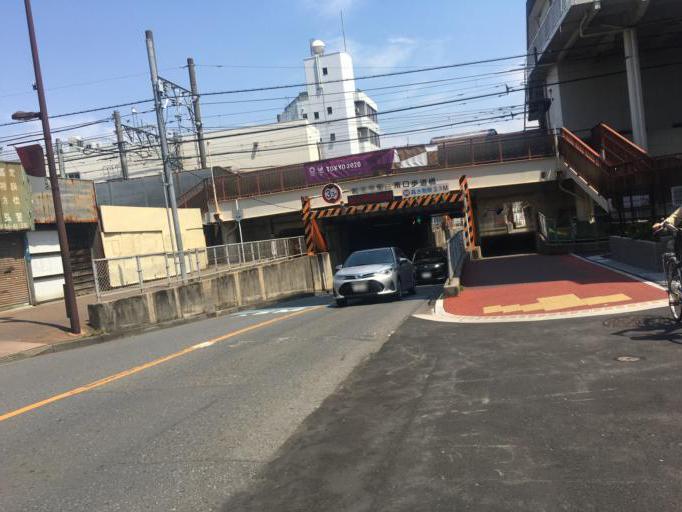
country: JP
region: Saitama
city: Wako
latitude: 35.7885
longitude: 139.6115
